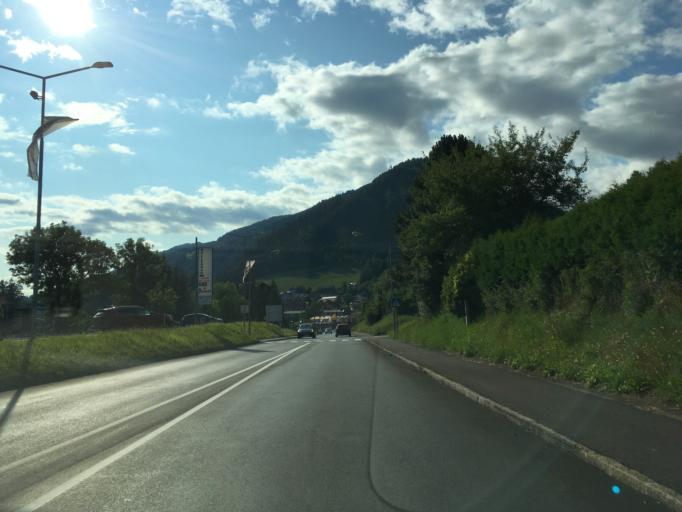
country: AT
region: Styria
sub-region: Politischer Bezirk Murau
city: Murau
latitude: 47.1132
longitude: 14.1776
